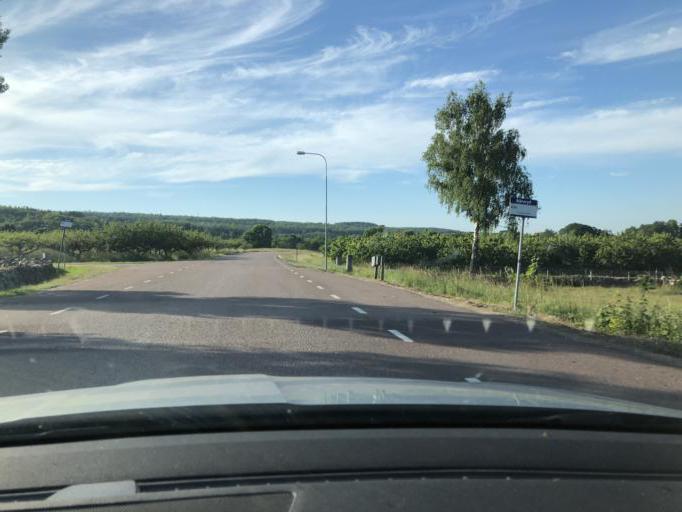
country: SE
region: Blekinge
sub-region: Solvesborgs Kommun
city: Soelvesborg
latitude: 56.1541
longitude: 14.6019
